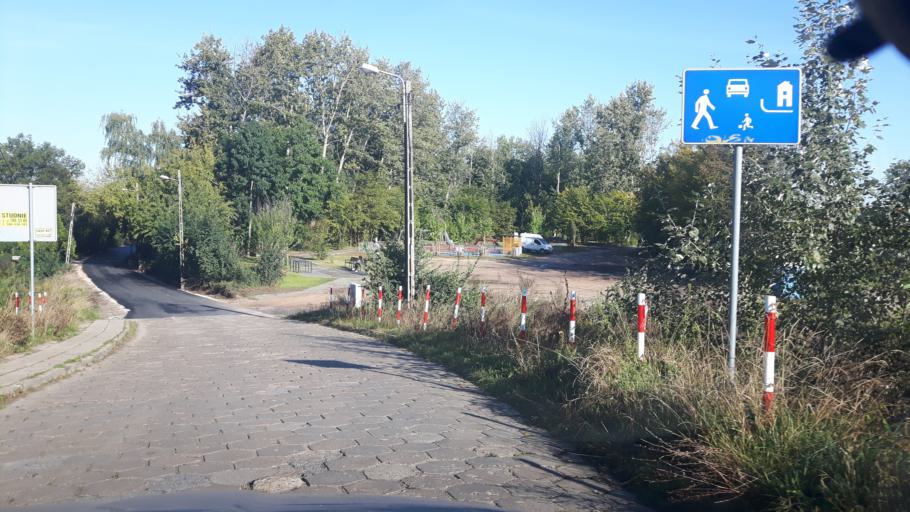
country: PL
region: Masovian Voivodeship
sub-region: Powiat legionowski
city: Stanislawow Pierwszy
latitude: 52.3576
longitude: 21.0328
